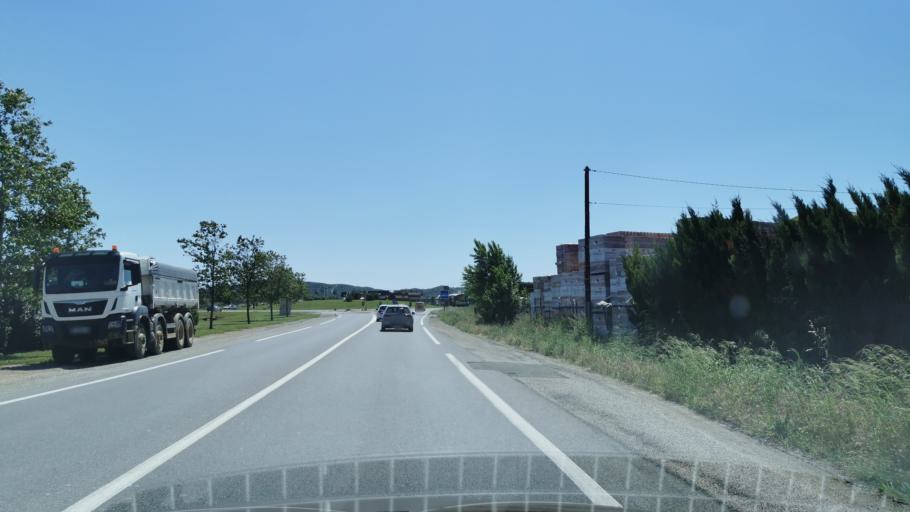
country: FR
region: Languedoc-Roussillon
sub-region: Departement de l'Aude
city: Nevian
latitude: 43.1846
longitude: 2.9319
